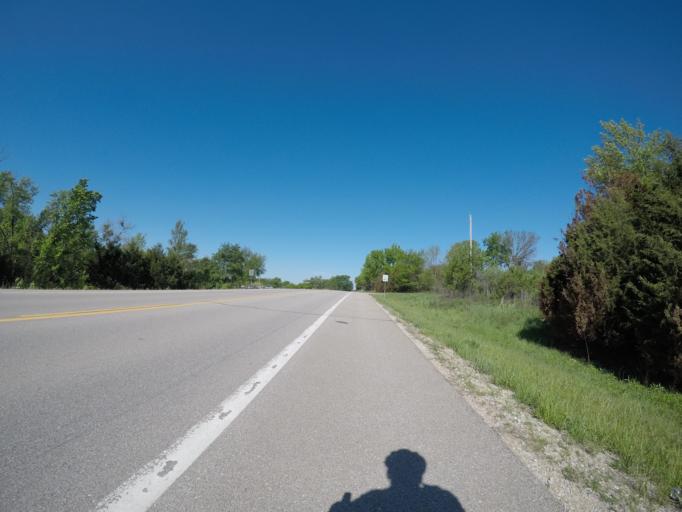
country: US
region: Kansas
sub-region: Douglas County
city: Lawrence
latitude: 38.9713
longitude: -95.4519
